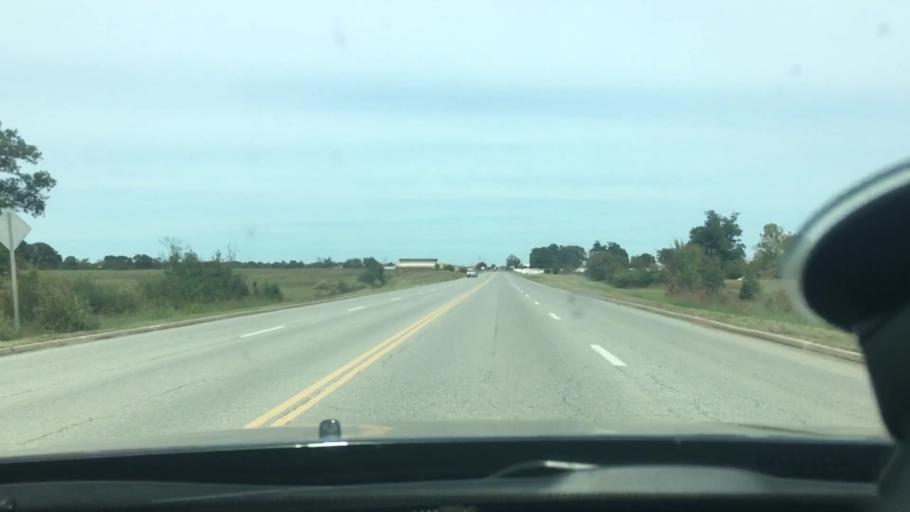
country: US
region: Oklahoma
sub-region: Atoka County
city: Atoka
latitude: 34.3862
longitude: -96.1455
